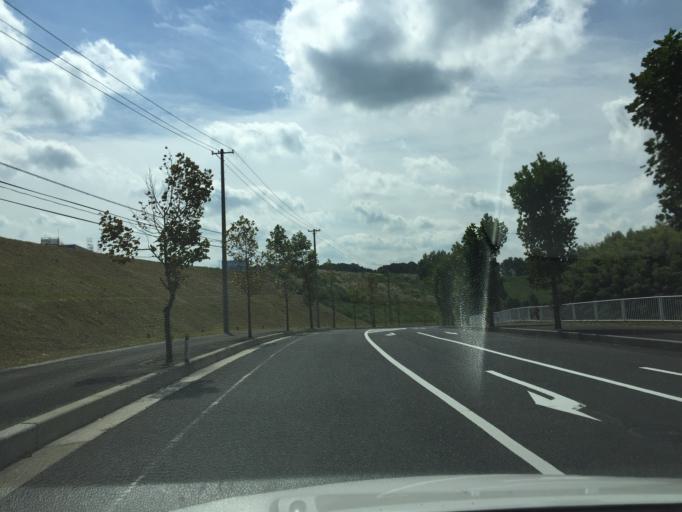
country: JP
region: Fukushima
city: Miharu
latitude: 37.4364
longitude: 140.5182
